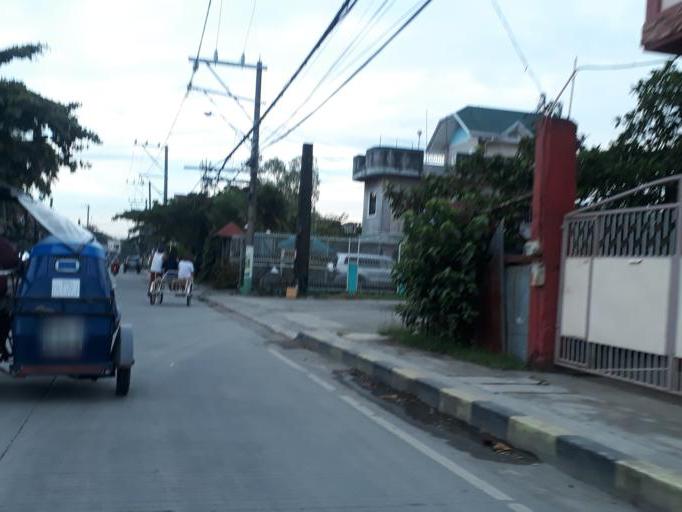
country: PH
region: Central Luzon
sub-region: Province of Bulacan
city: Obando
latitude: 14.7089
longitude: 120.9521
